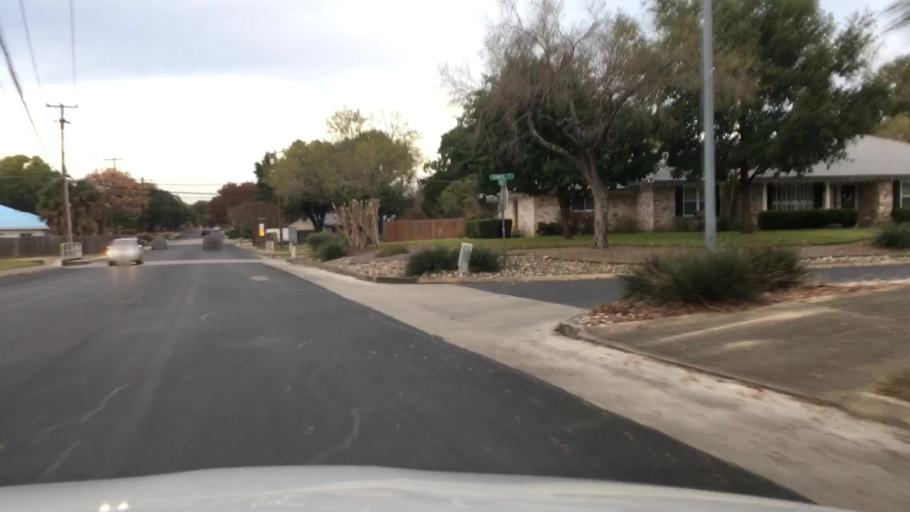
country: US
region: Texas
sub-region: Bexar County
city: Windcrest
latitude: 29.5128
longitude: -98.3842
